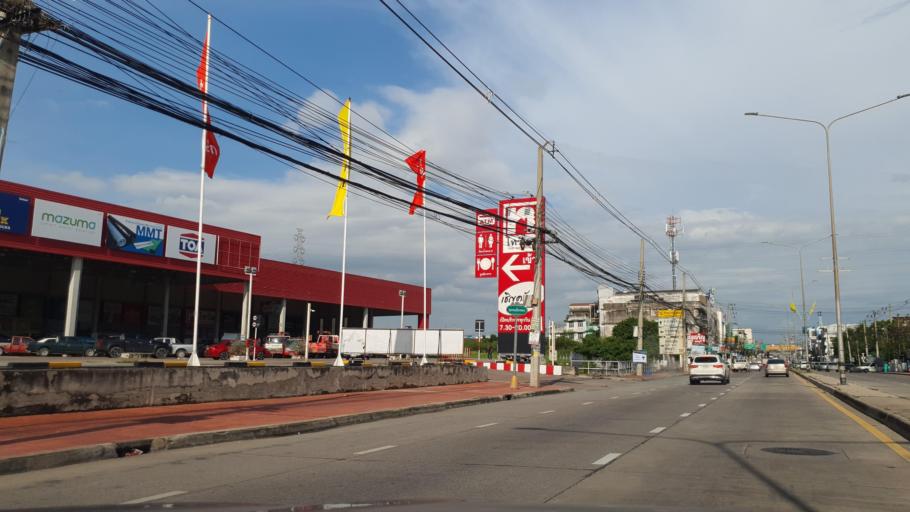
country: TH
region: Chon Buri
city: Chon Buri
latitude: 13.3560
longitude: 100.9988
